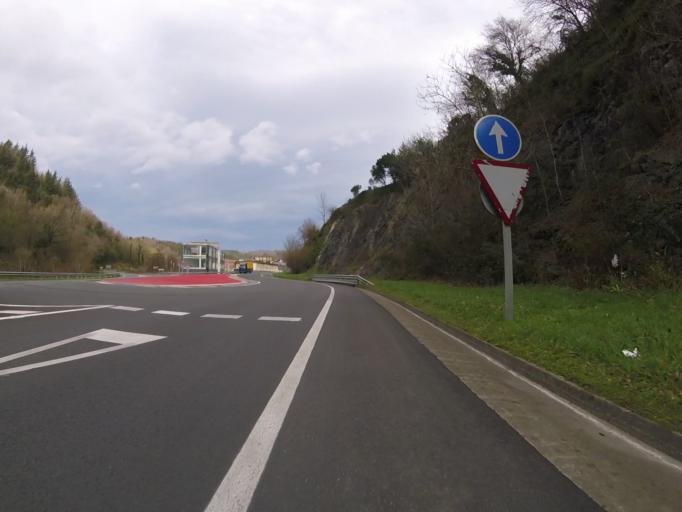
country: ES
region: Basque Country
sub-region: Provincia de Guipuzcoa
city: Cestona
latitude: 43.2514
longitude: -2.2607
